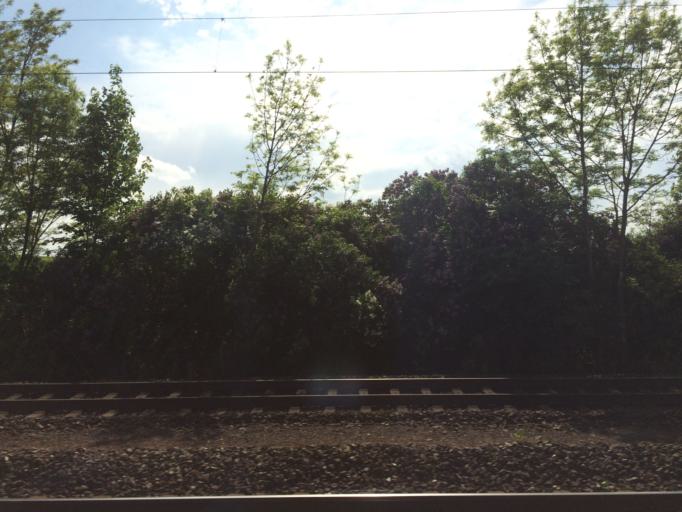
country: DE
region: Bavaria
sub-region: Regierungsbezirk Unterfranken
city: Biebelried
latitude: 49.7890
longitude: 10.0895
